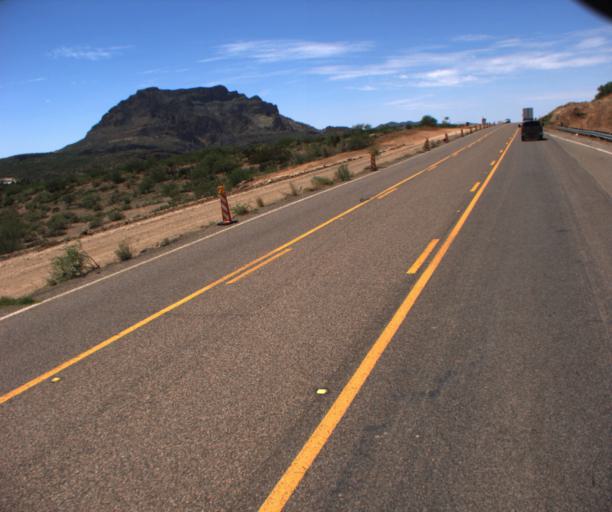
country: US
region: Arizona
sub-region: Pinal County
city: Superior
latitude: 33.2852
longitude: -111.1211
